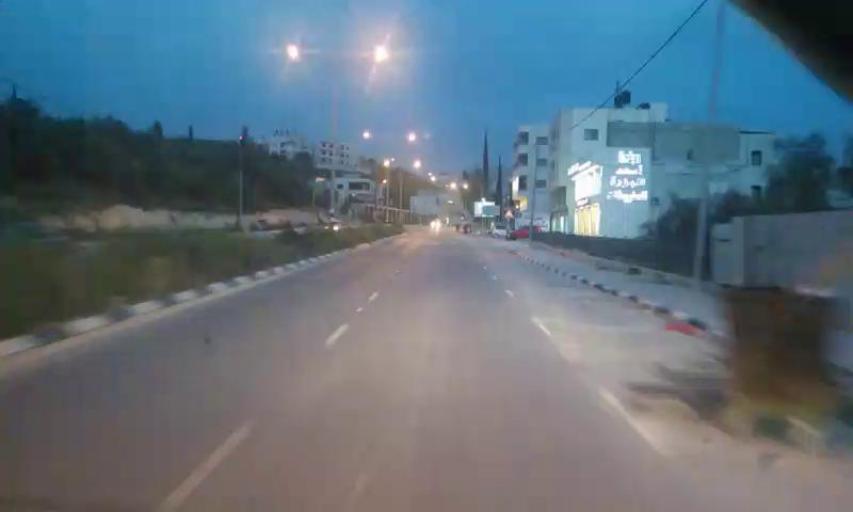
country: PS
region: West Bank
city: Bayt Iba
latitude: 32.2418
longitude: 35.2042
